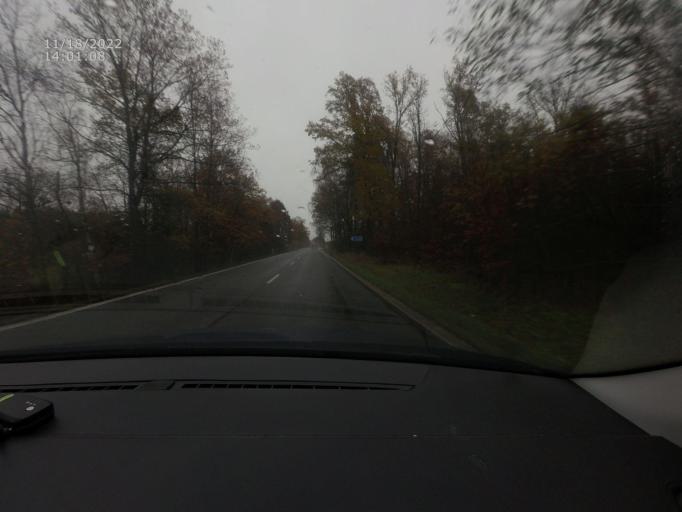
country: CZ
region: Jihocesky
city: Mirotice
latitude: 49.3511
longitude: 14.0341
